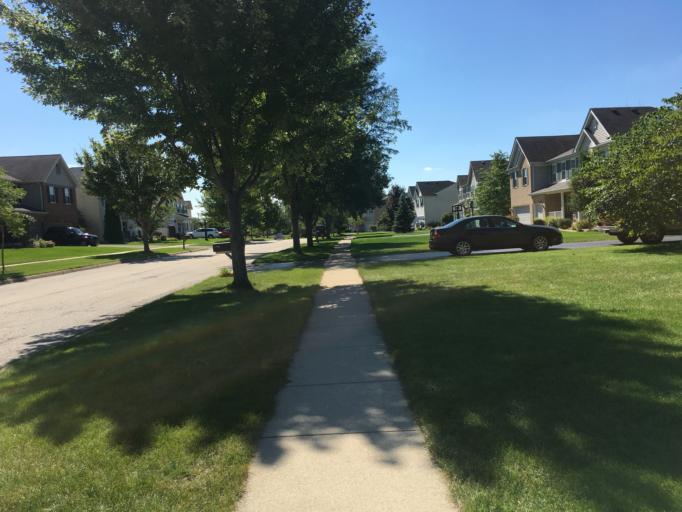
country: US
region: Illinois
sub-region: McHenry County
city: Lakewood
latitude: 42.2191
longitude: -88.3684
